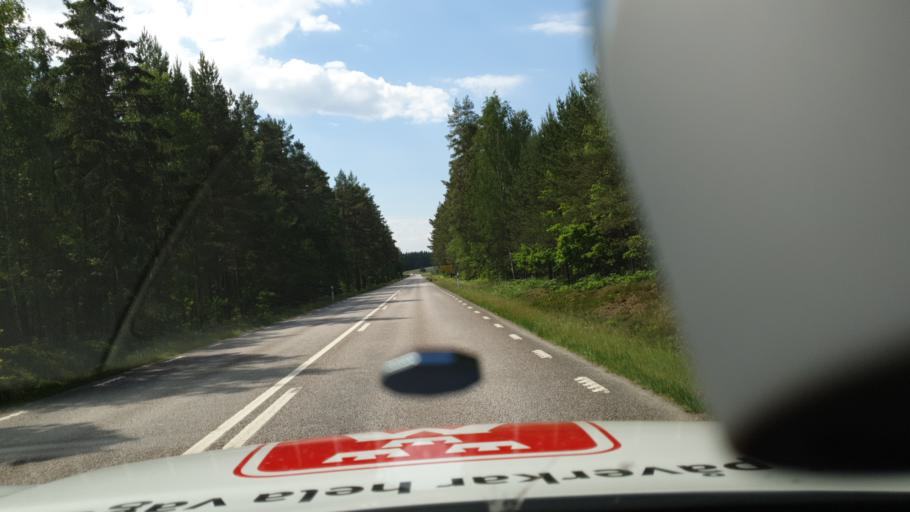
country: SE
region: Vaestra Goetaland
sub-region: Hjo Kommun
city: Hjo
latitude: 58.1944
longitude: 14.2058
